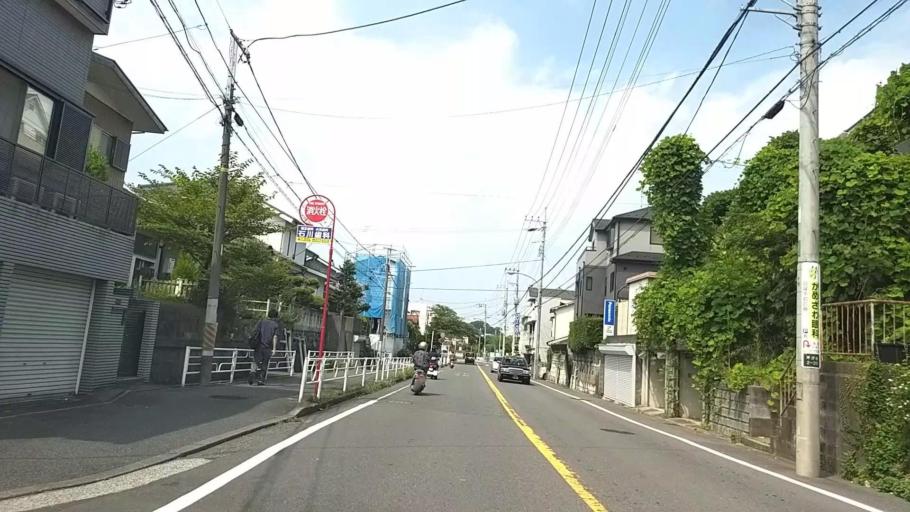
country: JP
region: Kanagawa
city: Yokohama
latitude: 35.4169
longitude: 139.5687
